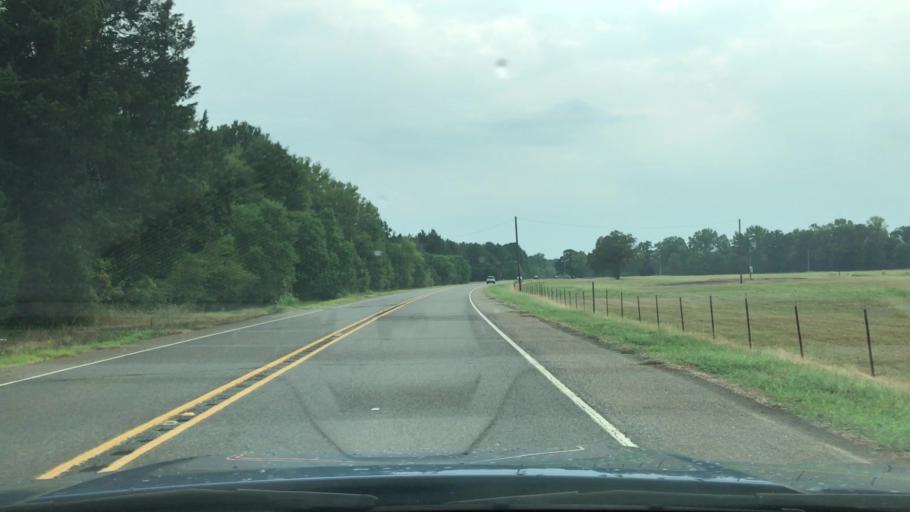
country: US
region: Texas
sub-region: Harrison County
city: Waskom
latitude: 32.4611
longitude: -94.0274
